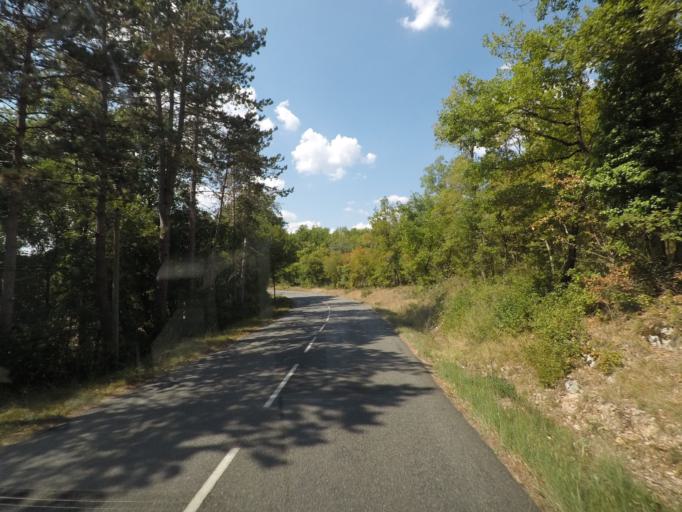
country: FR
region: Midi-Pyrenees
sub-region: Departement du Lot
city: Cahors
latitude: 44.5530
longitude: 1.5878
